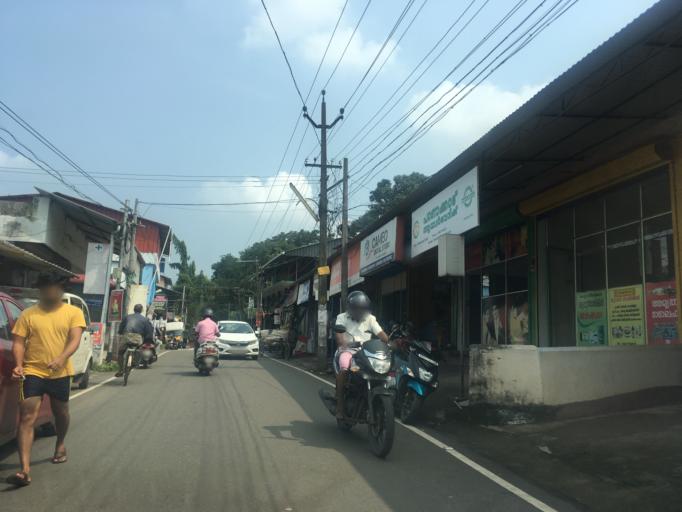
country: IN
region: Kerala
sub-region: Ernakulam
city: Elur
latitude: 10.0428
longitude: 76.3054
